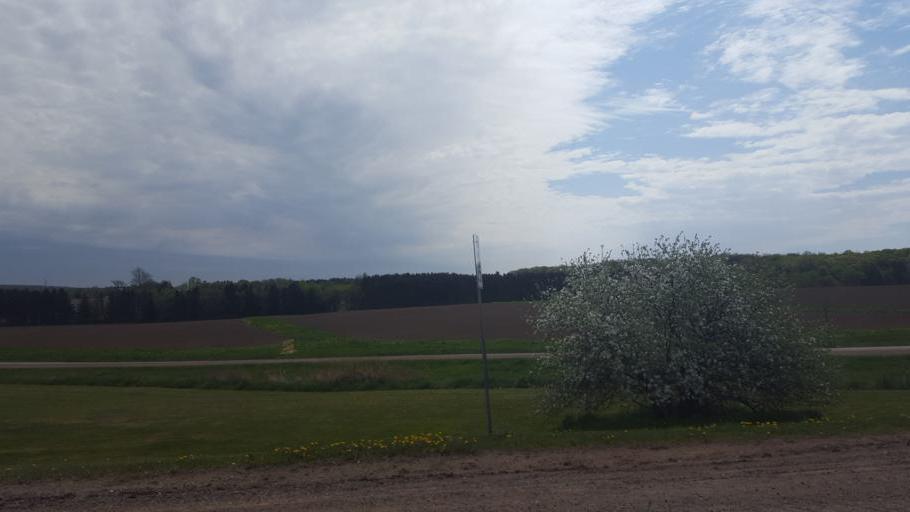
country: US
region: Wisconsin
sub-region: Clark County
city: Neillsville
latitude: 44.5802
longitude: -90.4564
